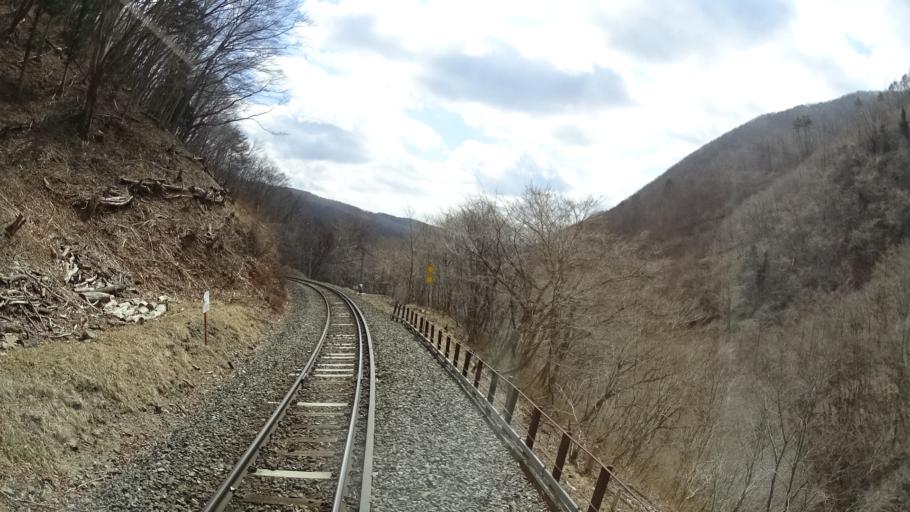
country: JP
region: Iwate
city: Tono
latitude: 39.2411
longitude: 141.6705
